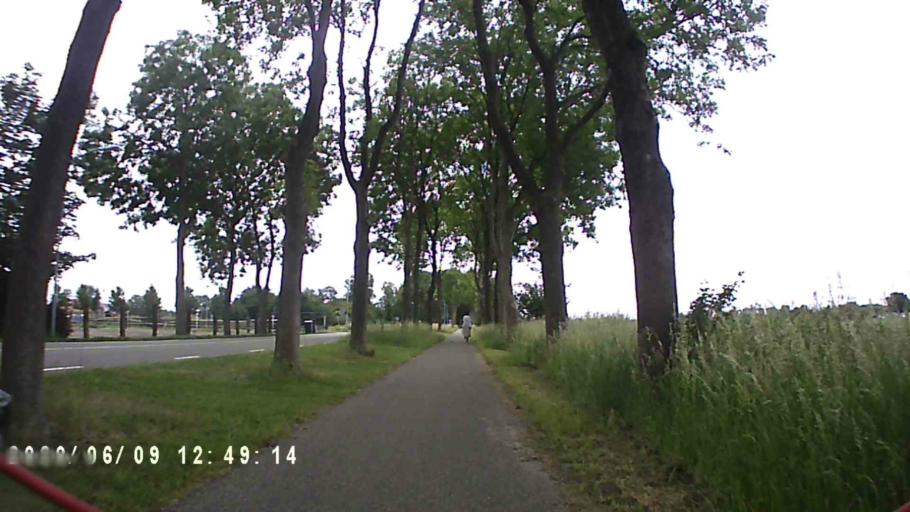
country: NL
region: Groningen
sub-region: Gemeente Haren
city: Haren
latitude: 53.2209
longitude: 6.6468
